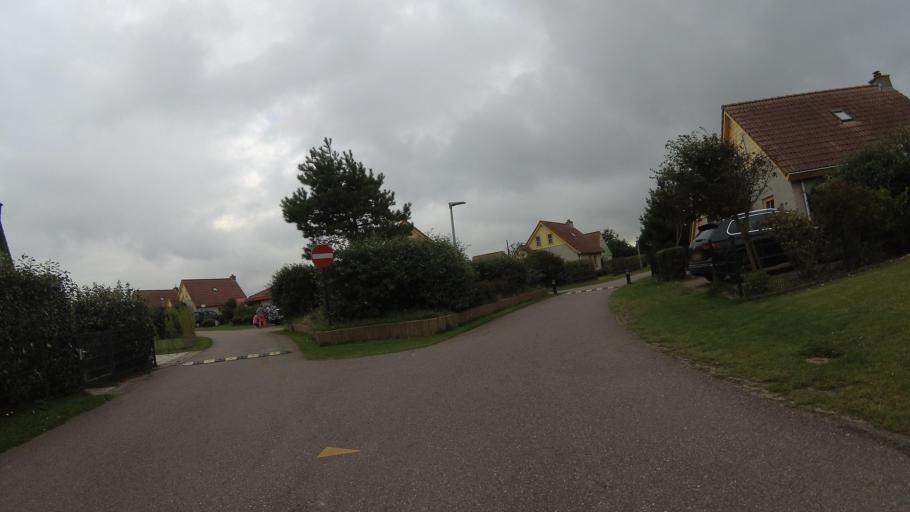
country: NL
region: North Holland
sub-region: Gemeente Den Helder
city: Den Helder
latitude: 52.8985
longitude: 4.7215
